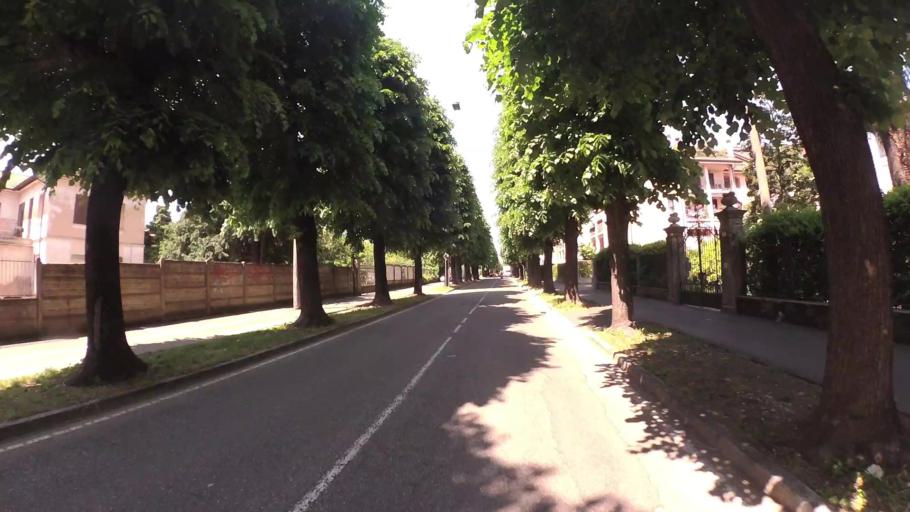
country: IT
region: Lombardy
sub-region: Provincia di Varese
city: Tradate
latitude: 45.7059
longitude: 8.9137
